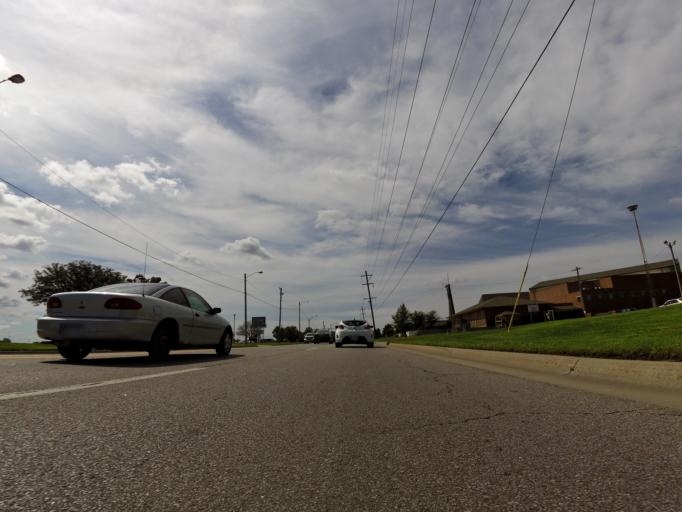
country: US
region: Kansas
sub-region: Sedgwick County
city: Bellaire
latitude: 37.7201
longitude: -97.2624
